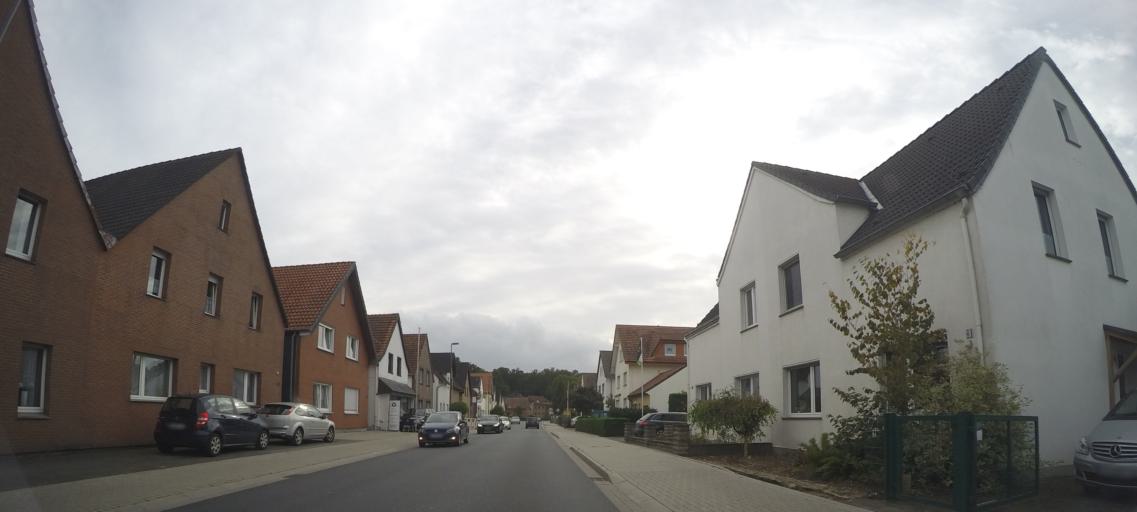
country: DE
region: North Rhine-Westphalia
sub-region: Regierungsbezirk Arnsberg
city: Lippstadt
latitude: 51.6871
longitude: 8.3684
